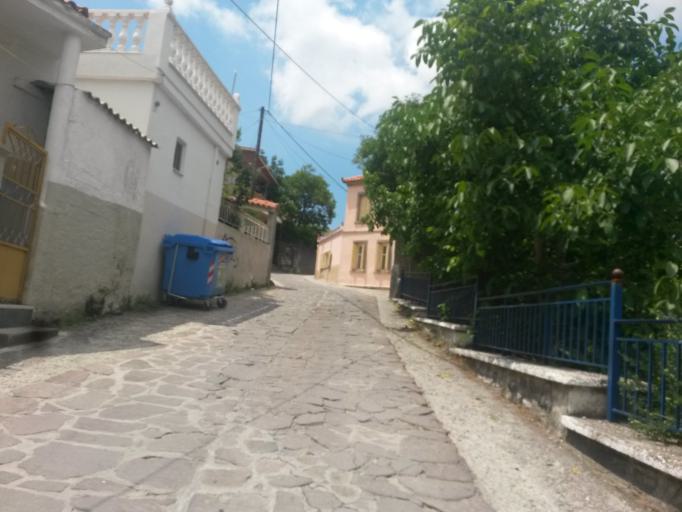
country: GR
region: North Aegean
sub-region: Nomos Lesvou
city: Petra
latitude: 39.2591
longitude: 26.0731
